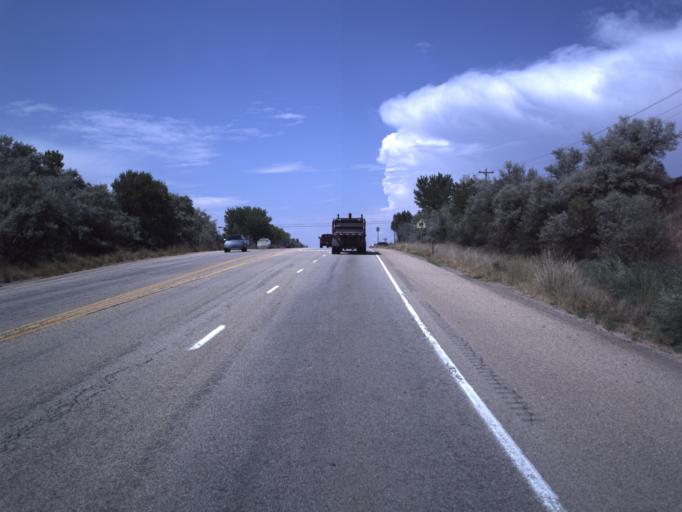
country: US
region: Utah
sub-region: Duchesne County
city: Roosevelt
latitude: 40.3019
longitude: -109.8897
